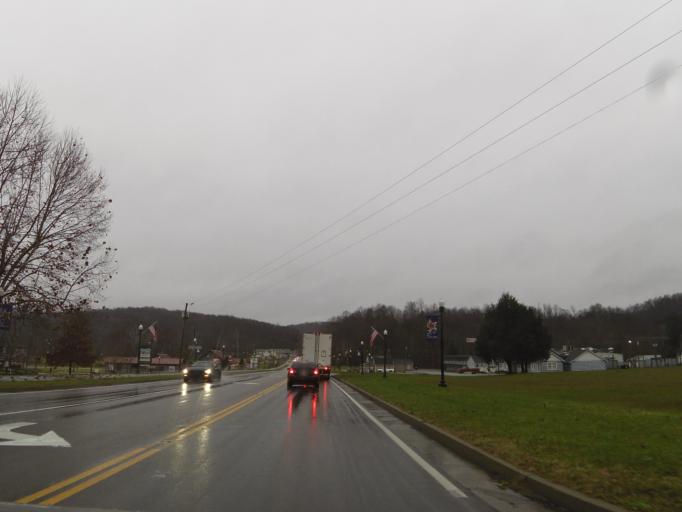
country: US
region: Kentucky
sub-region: Rockcastle County
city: Mount Vernon
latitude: 37.3874
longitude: -84.3320
